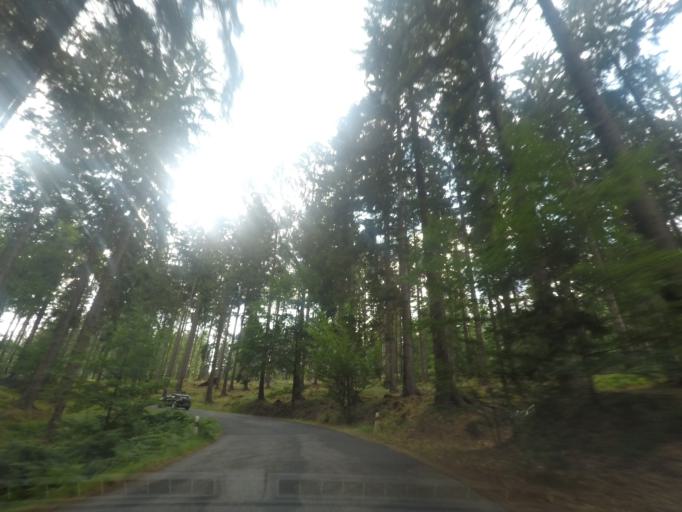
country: CZ
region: Ustecky
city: Mikulasovice
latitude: 50.8688
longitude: 14.3312
